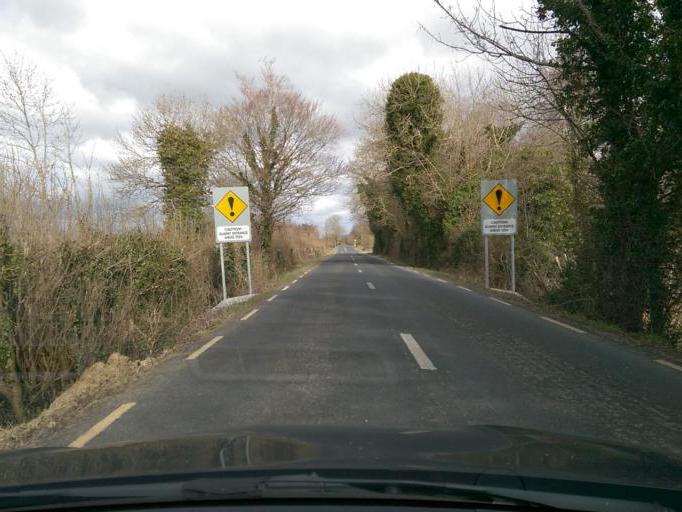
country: IE
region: Connaught
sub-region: County Galway
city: Ballinasloe
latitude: 53.3313
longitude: -8.2615
